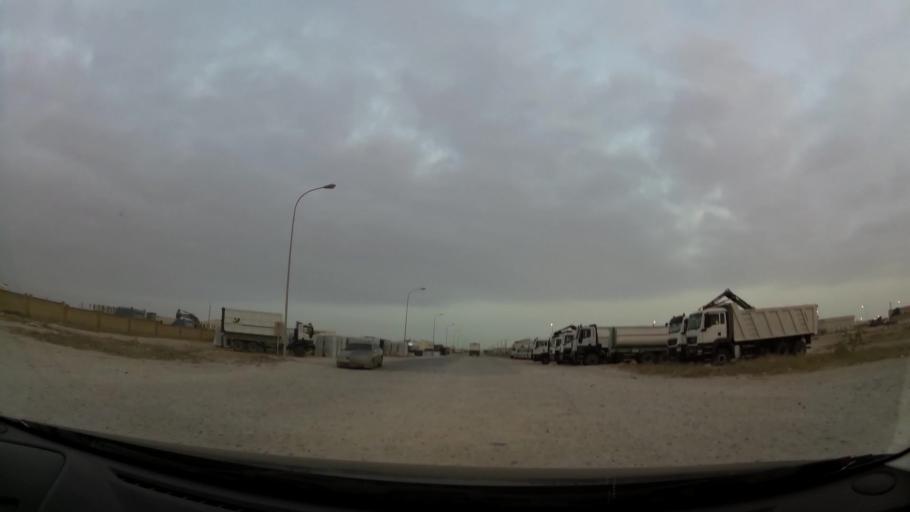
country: OM
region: Zufar
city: Salalah
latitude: 17.0368
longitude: 54.0420
